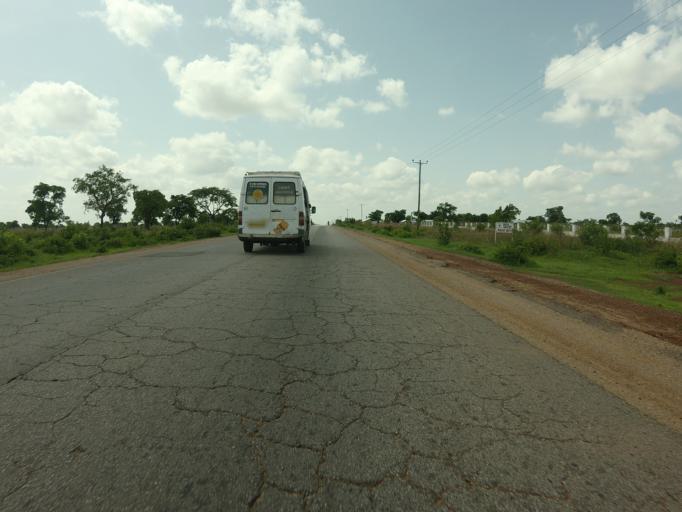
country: GH
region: Northern
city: Savelugu
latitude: 9.5864
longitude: -0.8330
